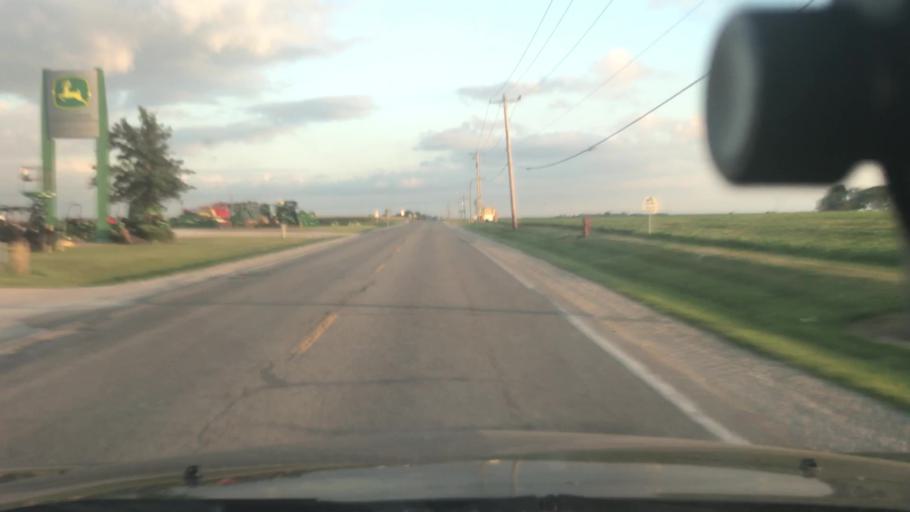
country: US
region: Illinois
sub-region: Washington County
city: Okawville
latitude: 38.4206
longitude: -89.5506
